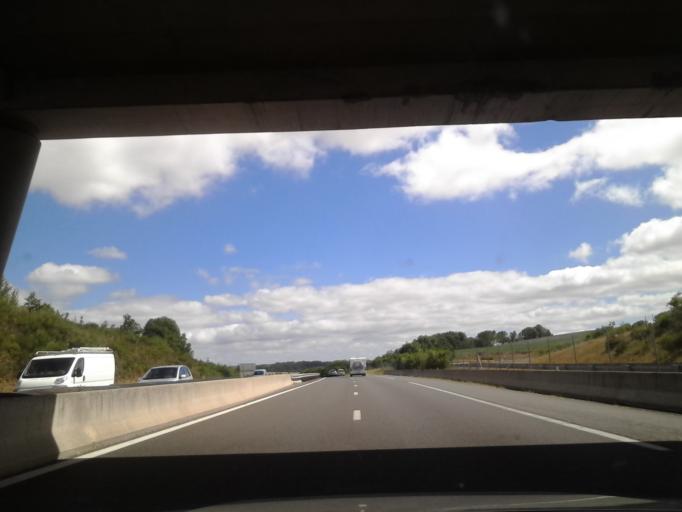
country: FR
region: Midi-Pyrenees
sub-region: Departement de l'Aveyron
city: Severac-le-Chateau
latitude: 44.2679
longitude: 3.0834
